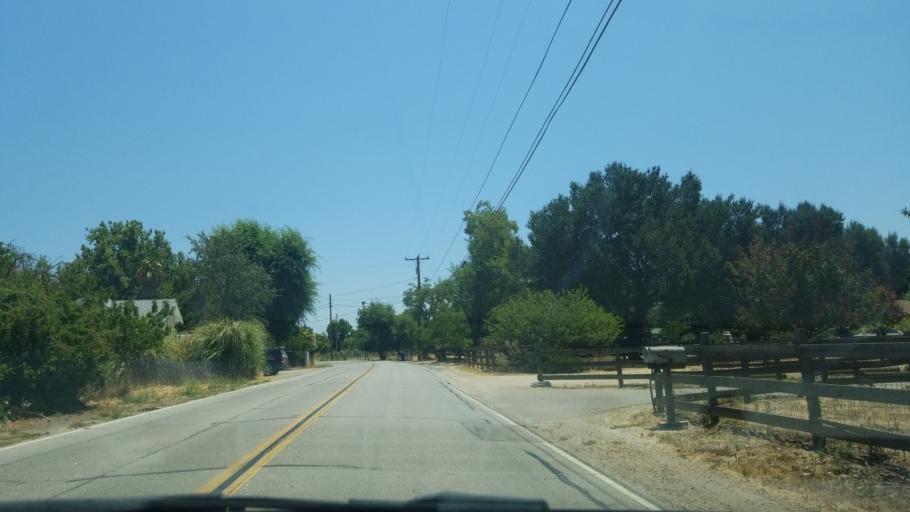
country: US
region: California
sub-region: San Luis Obispo County
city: Atascadero
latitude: 35.4938
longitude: -120.6480
